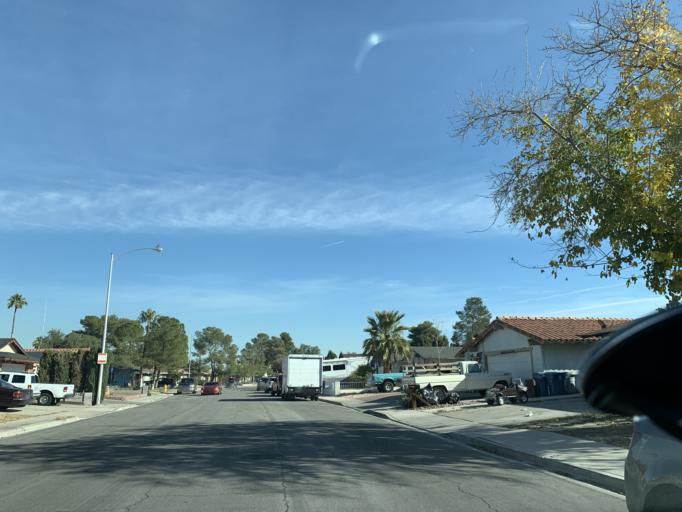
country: US
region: Nevada
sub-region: Clark County
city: Spring Valley
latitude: 36.1039
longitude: -115.2291
